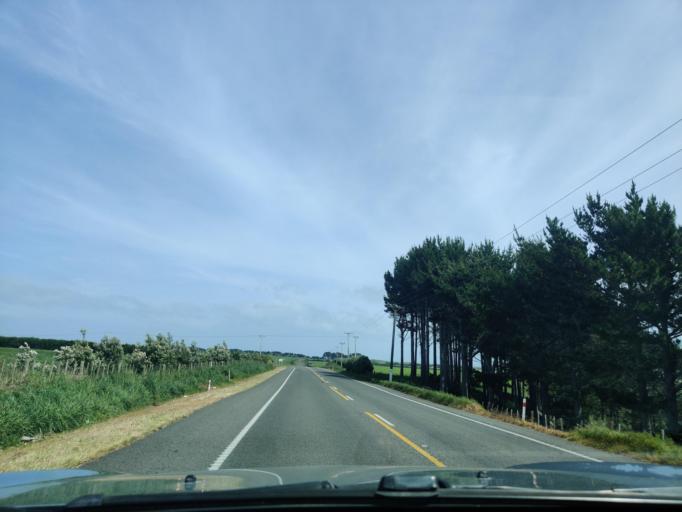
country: NZ
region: Taranaki
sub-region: South Taranaki District
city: Patea
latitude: -39.7201
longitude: 174.4472
